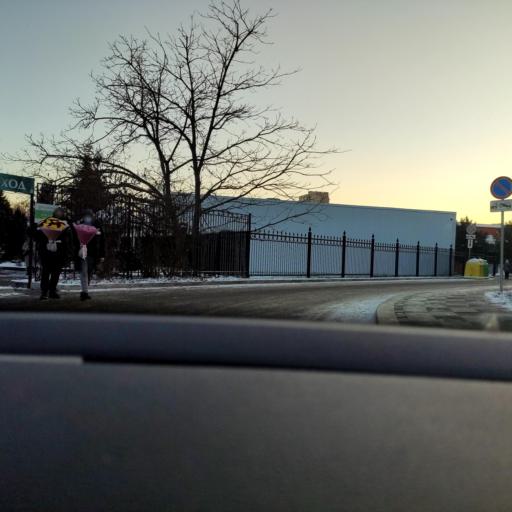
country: RU
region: Moskovskaya
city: Bogorodskoye
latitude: 55.8041
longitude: 37.7334
